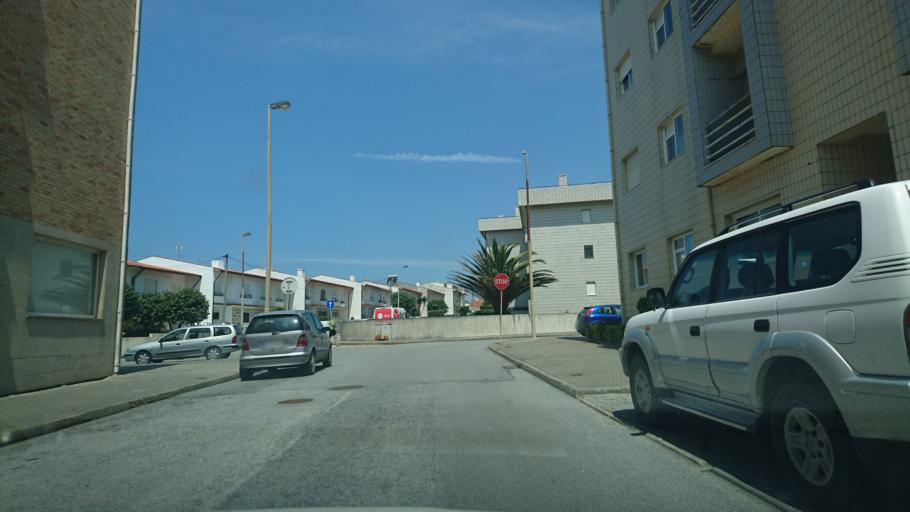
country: PT
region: Porto
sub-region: Matosinhos
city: Lavra
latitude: 41.2737
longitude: -8.7253
